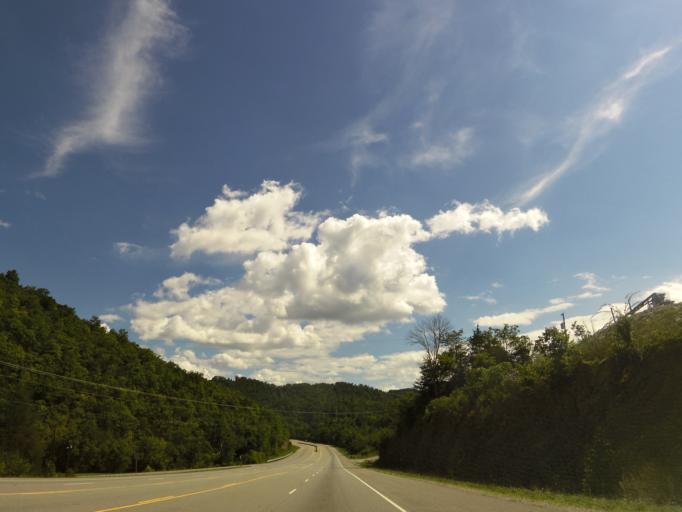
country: US
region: Tennessee
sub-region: Grainger County
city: Rutledge
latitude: 36.3851
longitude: -83.4473
